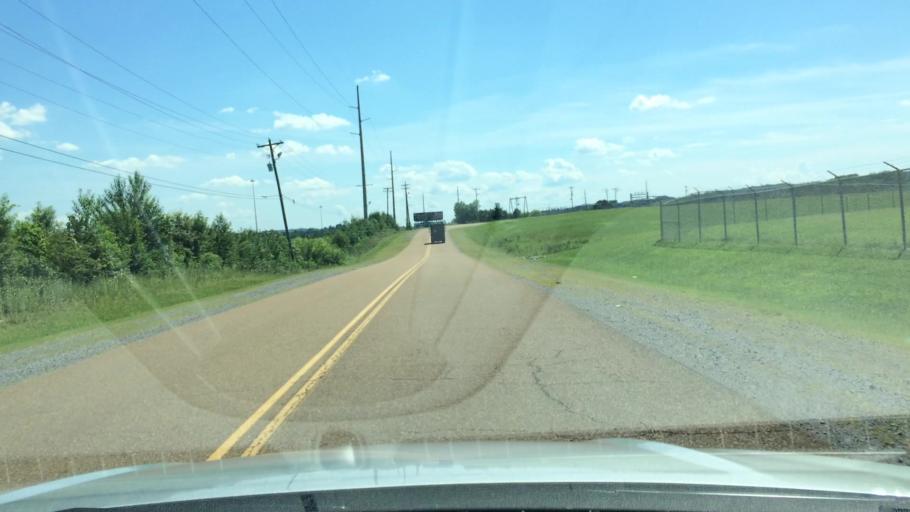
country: US
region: Tennessee
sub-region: McMinn County
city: Athens
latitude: 35.4730
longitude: -84.6430
